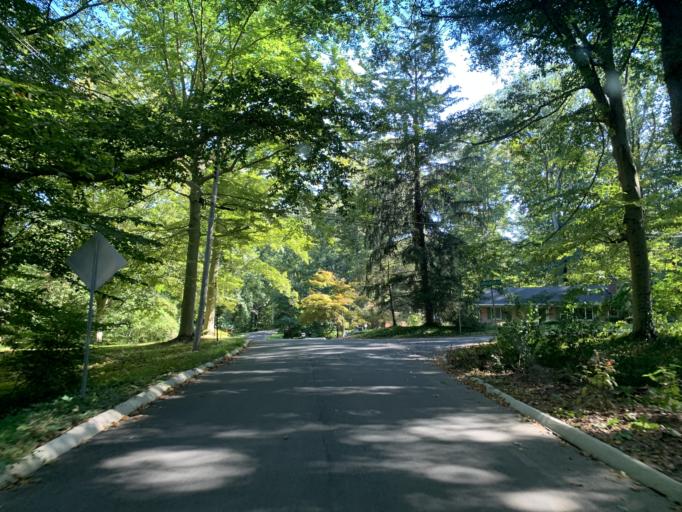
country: US
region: Maryland
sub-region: Harford County
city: South Bel Air
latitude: 39.5262
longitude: -76.3289
